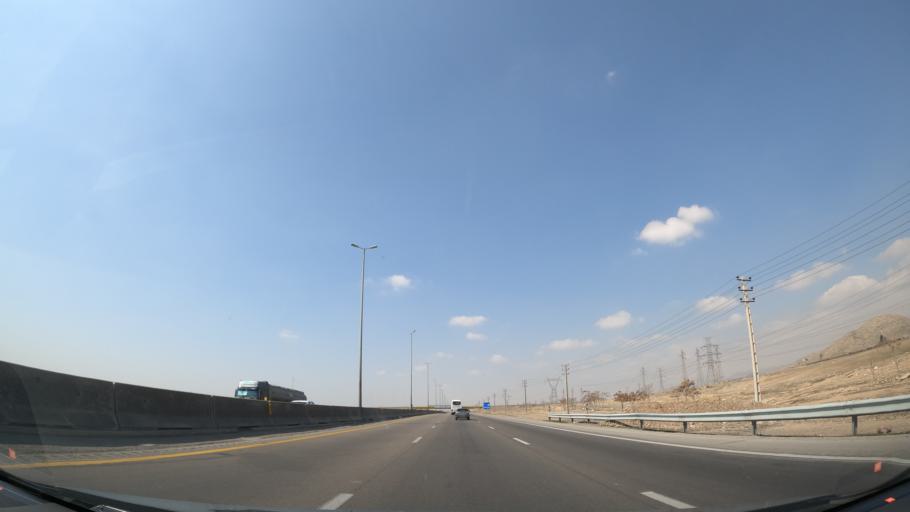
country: IR
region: Qazvin
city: Abyek
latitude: 36.0625
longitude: 50.4941
